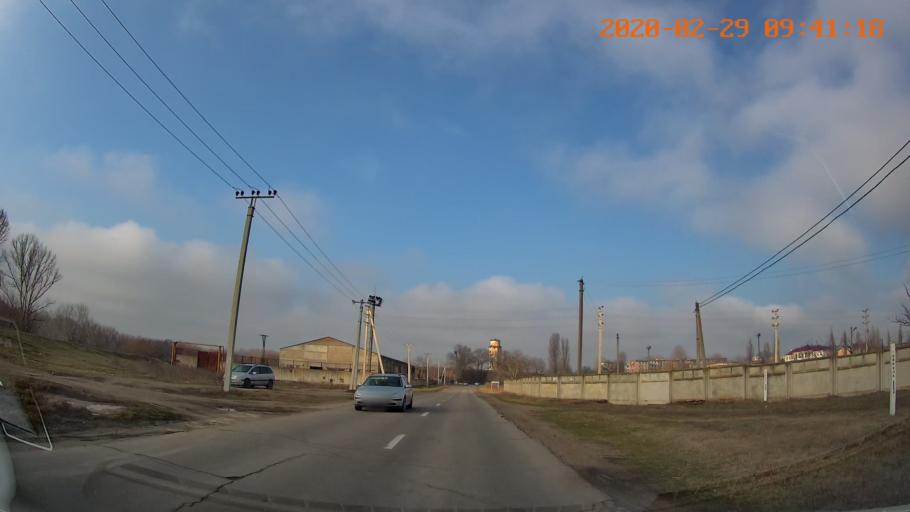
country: MD
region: Telenesti
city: Crasnoe
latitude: 46.6367
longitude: 29.8333
